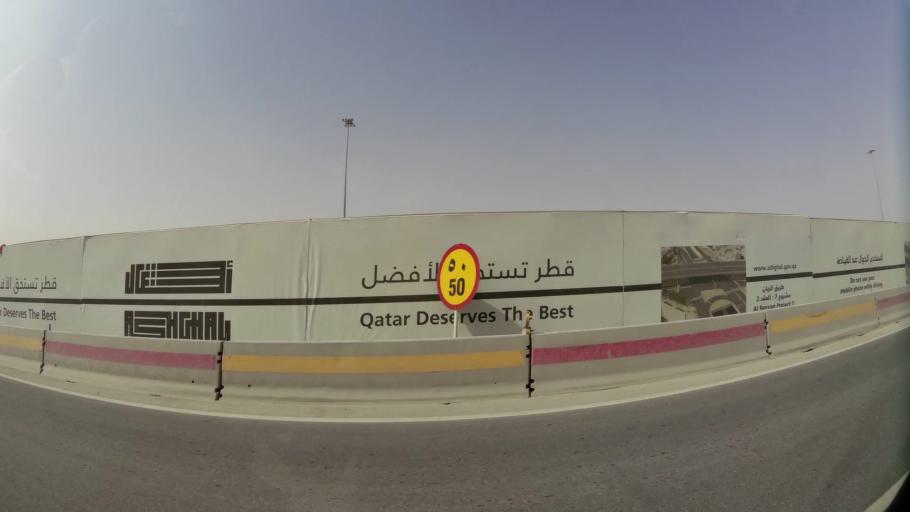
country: QA
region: Baladiyat ad Dawhah
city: Doha
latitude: 25.2911
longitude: 51.4779
